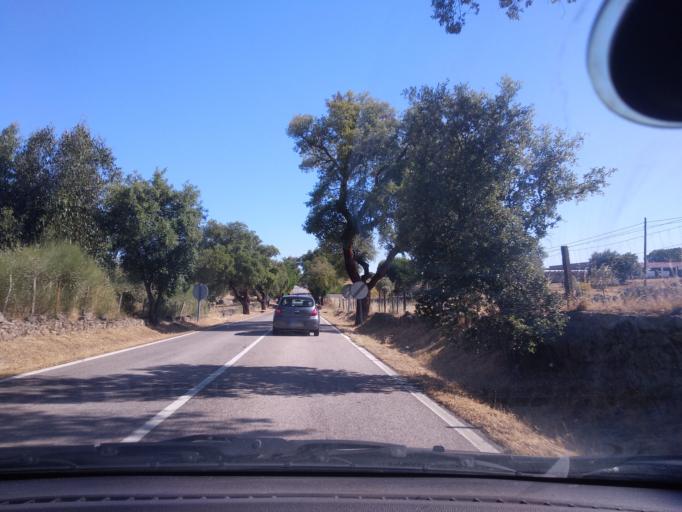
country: PT
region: Portalegre
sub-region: Nisa
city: Nisa
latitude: 39.4821
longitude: -7.6361
